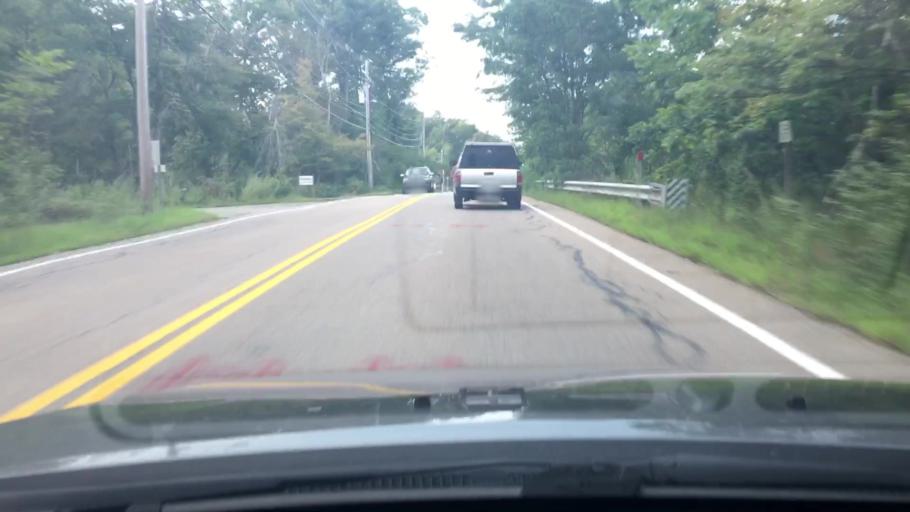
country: US
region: Massachusetts
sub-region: Middlesex County
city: Hopkinton
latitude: 42.1929
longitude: -71.5402
